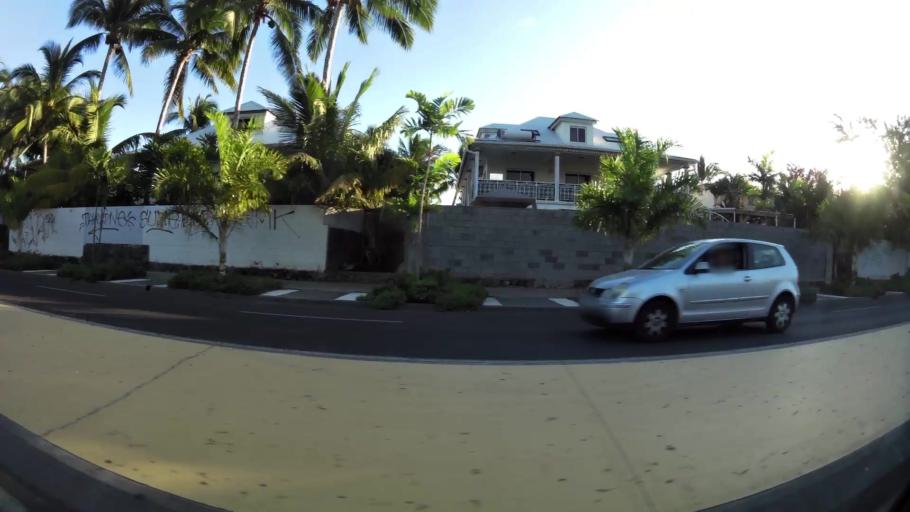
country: RE
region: Reunion
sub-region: Reunion
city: Trois-Bassins
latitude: -21.0837
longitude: 55.2314
